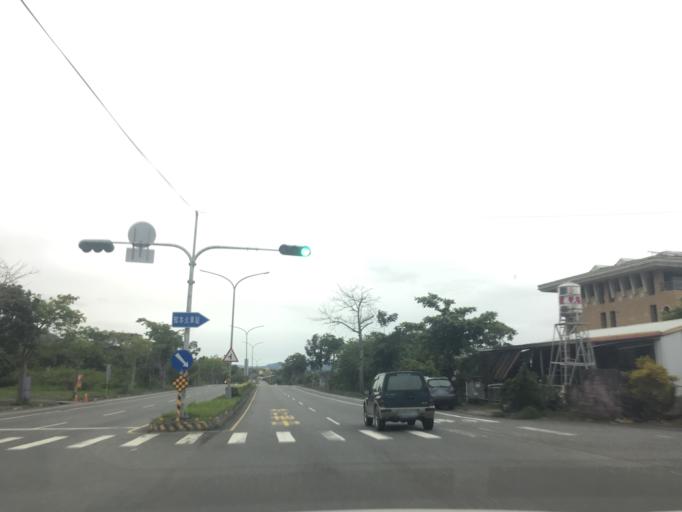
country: TW
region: Taiwan
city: Taitung City
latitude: 22.7207
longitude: 121.0536
